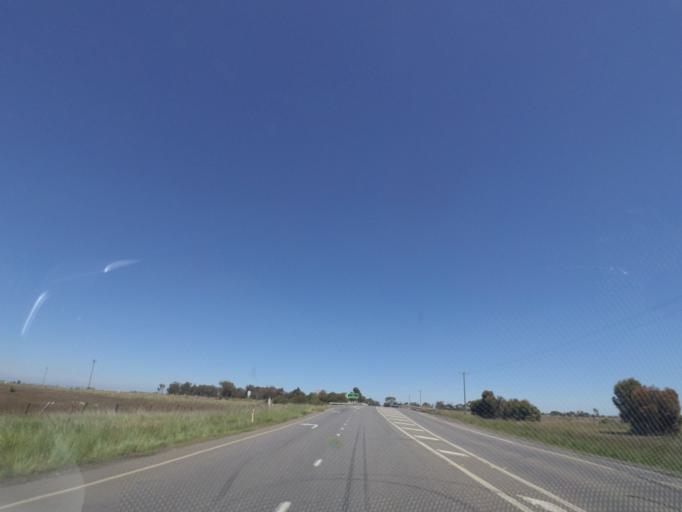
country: AU
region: Victoria
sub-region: Melton
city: Brookfield
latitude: -37.6855
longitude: 144.5027
